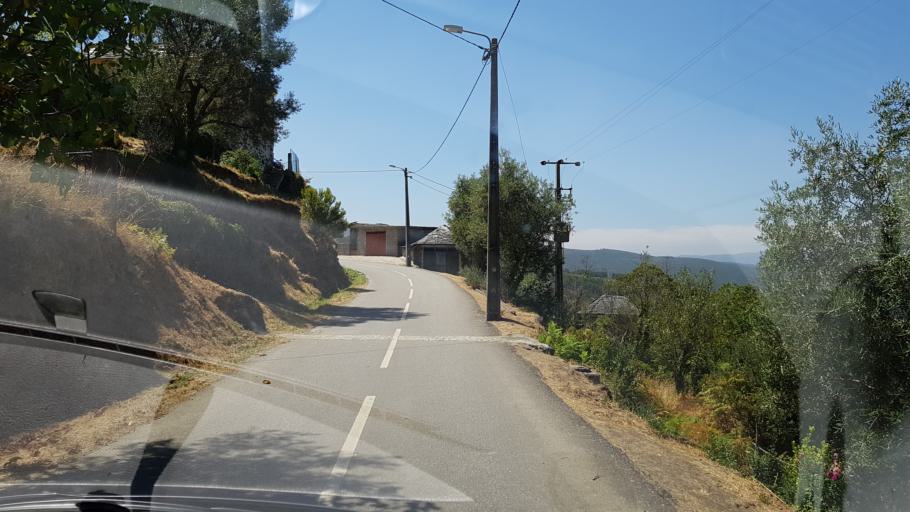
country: PT
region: Vila Real
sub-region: Mondim de Basto
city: Mondim de Basto
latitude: 41.3365
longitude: -7.8918
